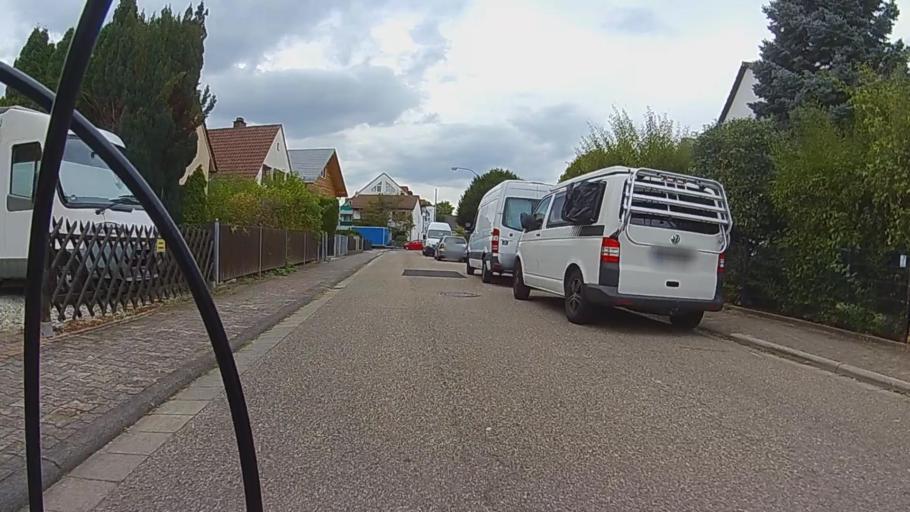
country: DE
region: Hesse
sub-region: Regierungsbezirk Darmstadt
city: Bad Homburg vor der Hoehe
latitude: 50.2047
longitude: 8.6055
